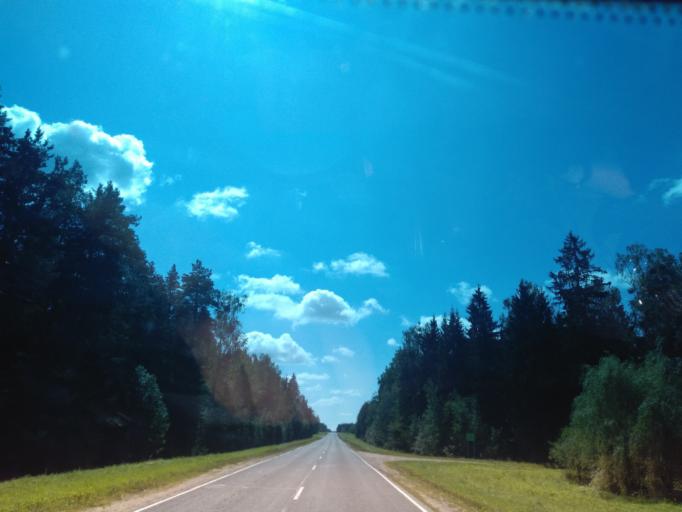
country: BY
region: Minsk
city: Uzda
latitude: 53.3416
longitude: 27.2283
